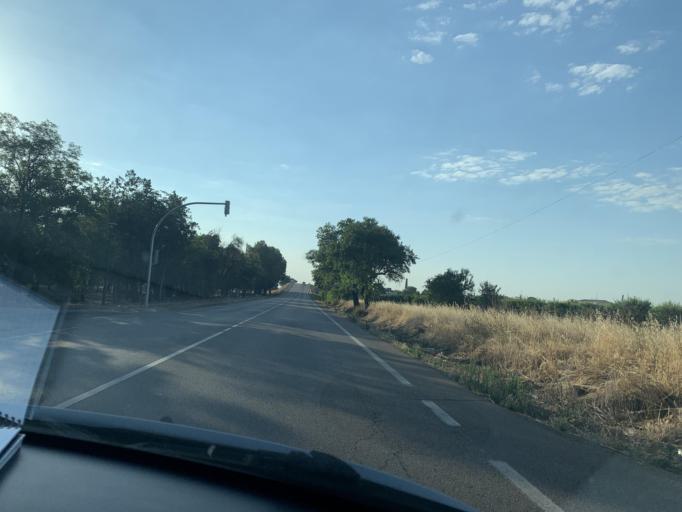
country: ES
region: Castille-La Mancha
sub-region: Provincia de Ciudad Real
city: Argamasilla de Alba
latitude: 39.1724
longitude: -3.2364
